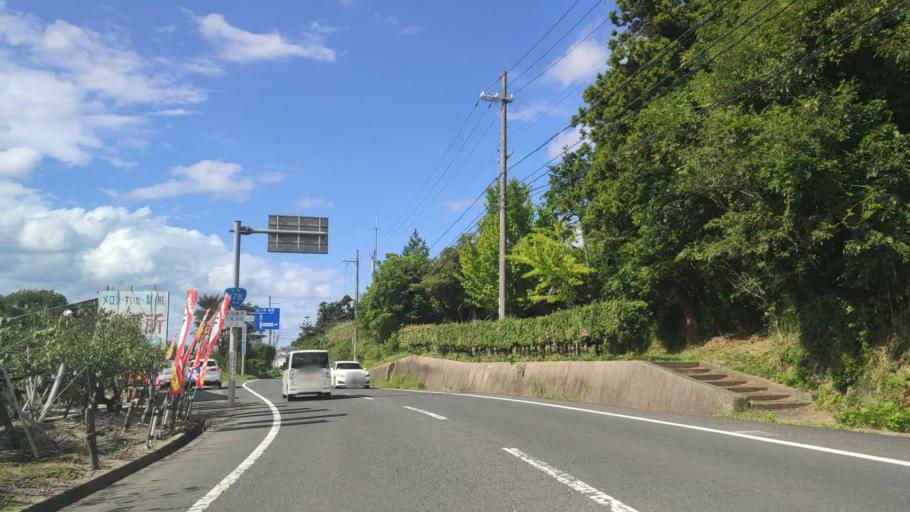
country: JP
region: Hyogo
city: Toyooka
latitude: 35.6409
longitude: 134.9458
